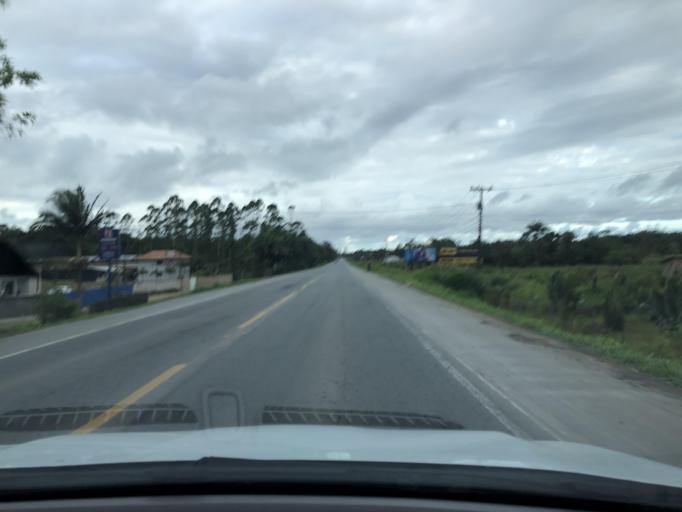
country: BR
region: Santa Catarina
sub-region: Joinville
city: Joinville
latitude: -26.4162
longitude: -48.7705
